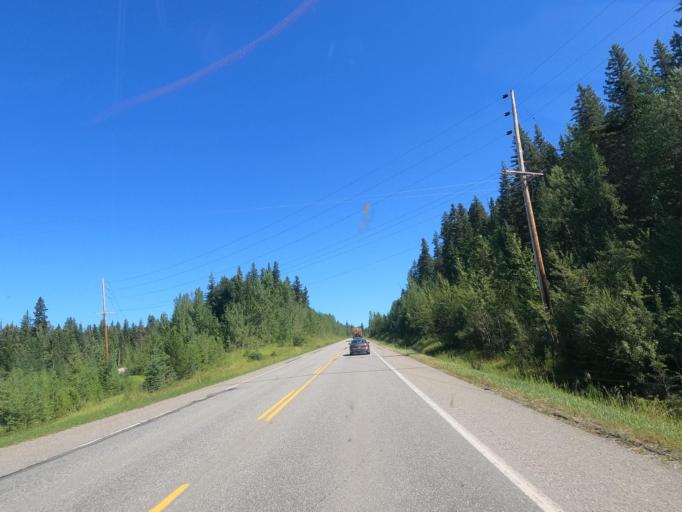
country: CA
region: British Columbia
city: Quesnel
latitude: 53.0591
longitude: -122.4481
